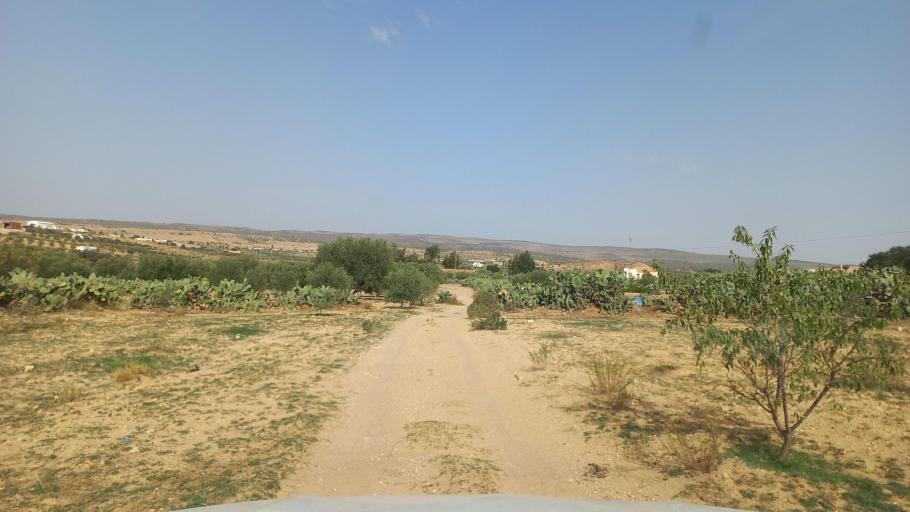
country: TN
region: Al Qasrayn
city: Kasserine
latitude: 35.2981
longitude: 8.9596
